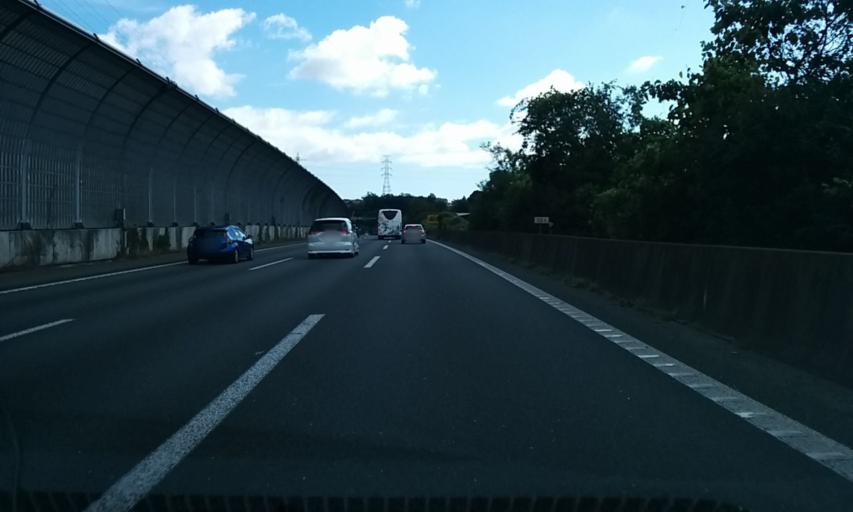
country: JP
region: Hyogo
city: Takarazuka
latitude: 34.8183
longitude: 135.3434
